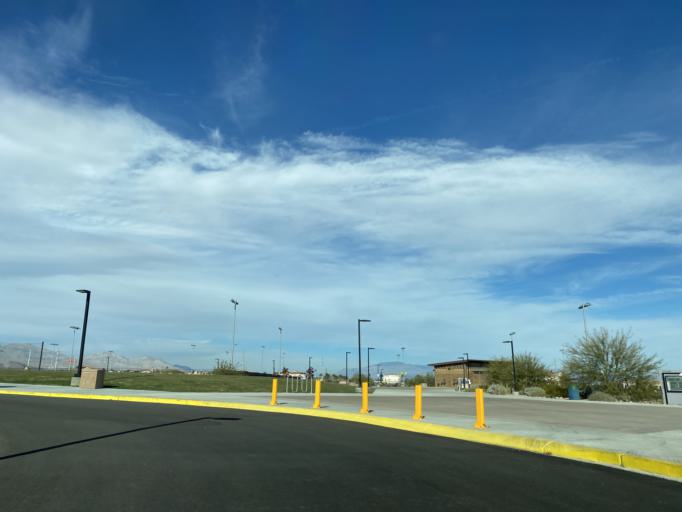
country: US
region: Nevada
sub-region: Clark County
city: Enterprise
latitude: 36.0496
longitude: -115.2743
